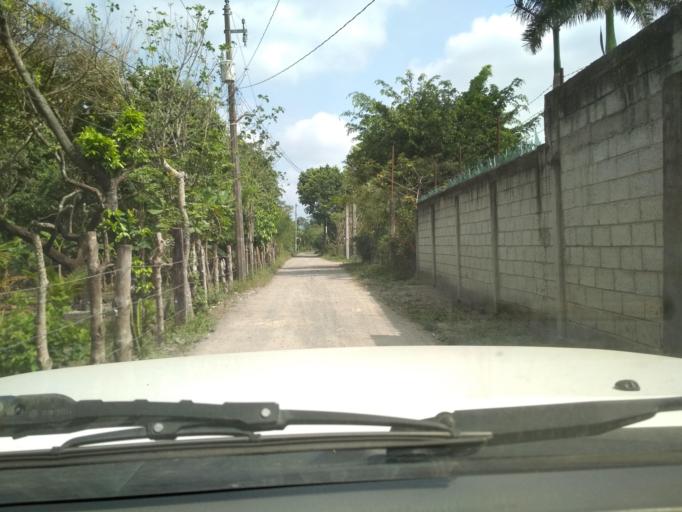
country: MX
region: Veracruz
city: El Tejar
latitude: 19.0791
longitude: -96.1699
